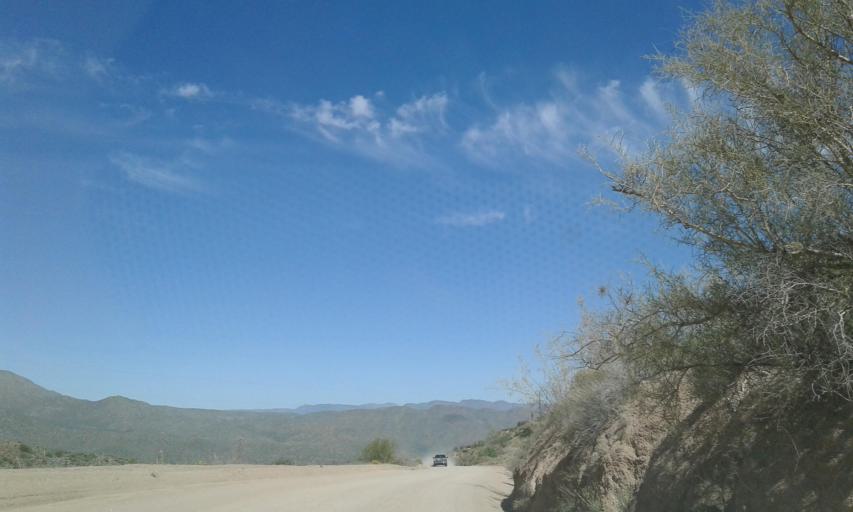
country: US
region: Arizona
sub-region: Gila County
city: Tonto Basin
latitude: 33.5751
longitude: -111.2296
